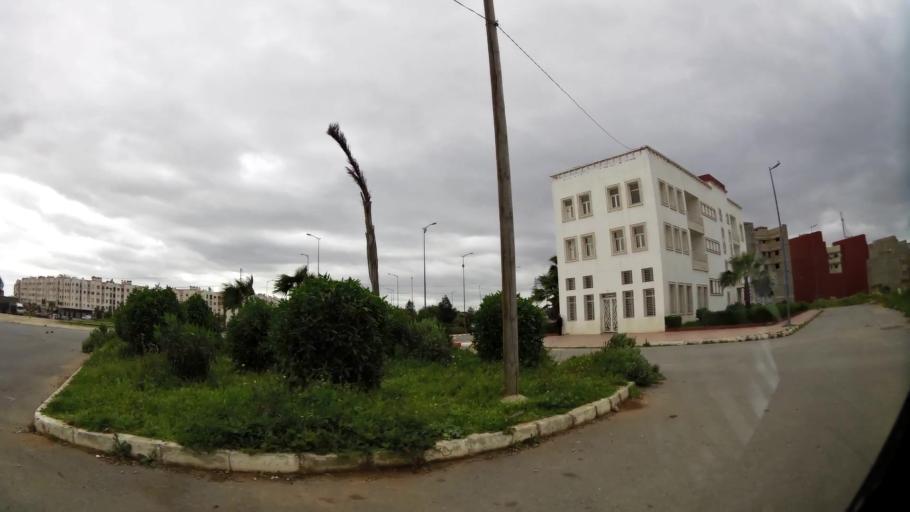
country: MA
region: Grand Casablanca
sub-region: Mediouna
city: Tit Mellil
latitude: 33.5521
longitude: -7.5306
